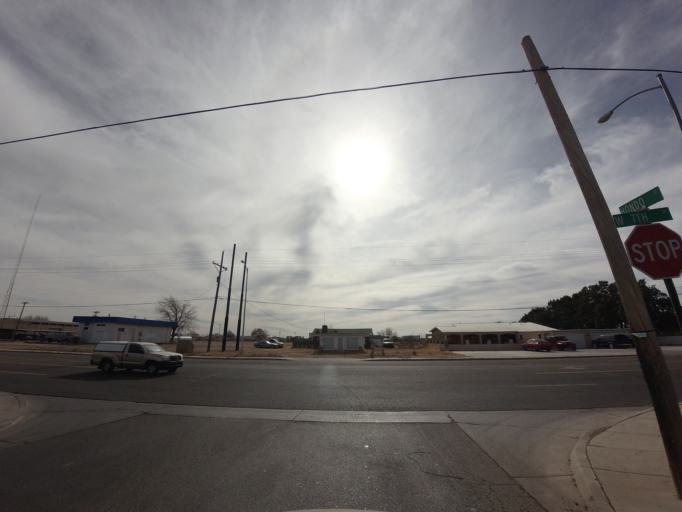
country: US
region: New Mexico
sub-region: Curry County
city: Clovis
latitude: 34.4048
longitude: -103.2375
